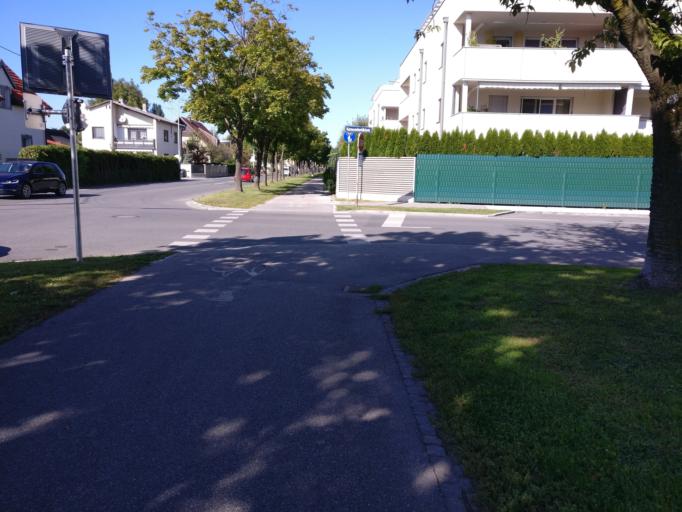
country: AT
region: Carinthia
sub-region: Klagenfurt am Woerthersee
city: Klagenfurt am Woerthersee
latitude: 46.6046
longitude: 14.2902
